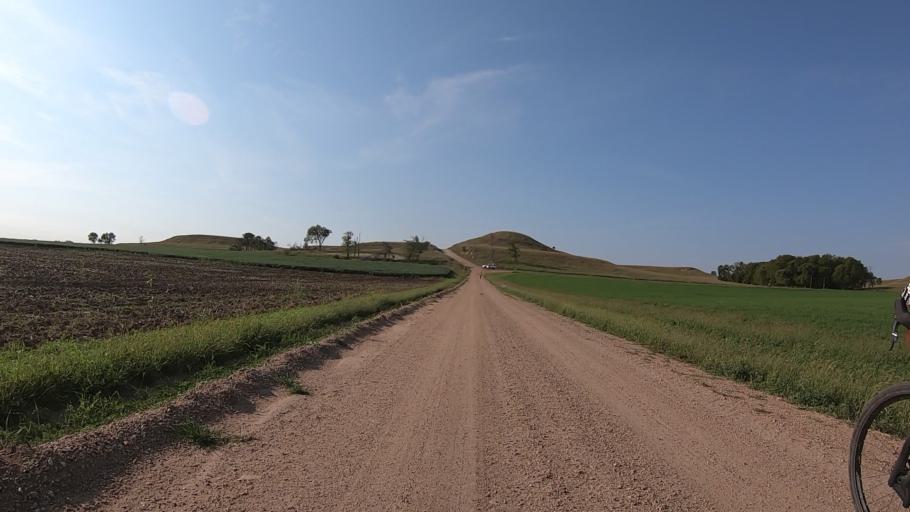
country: US
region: Kansas
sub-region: Marshall County
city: Blue Rapids
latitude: 39.6523
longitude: -96.8815
